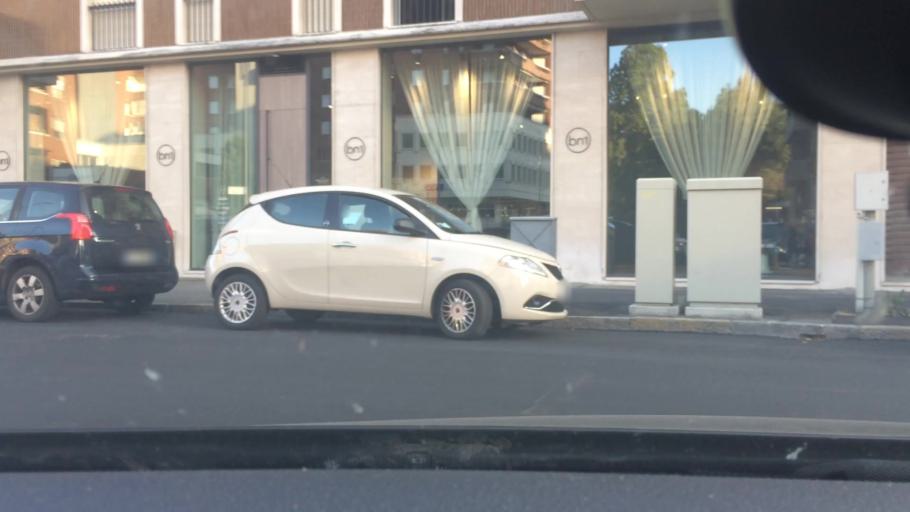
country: IT
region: Emilia-Romagna
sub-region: Provincia di Piacenza
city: Piacenza
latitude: 45.0452
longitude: 9.6866
